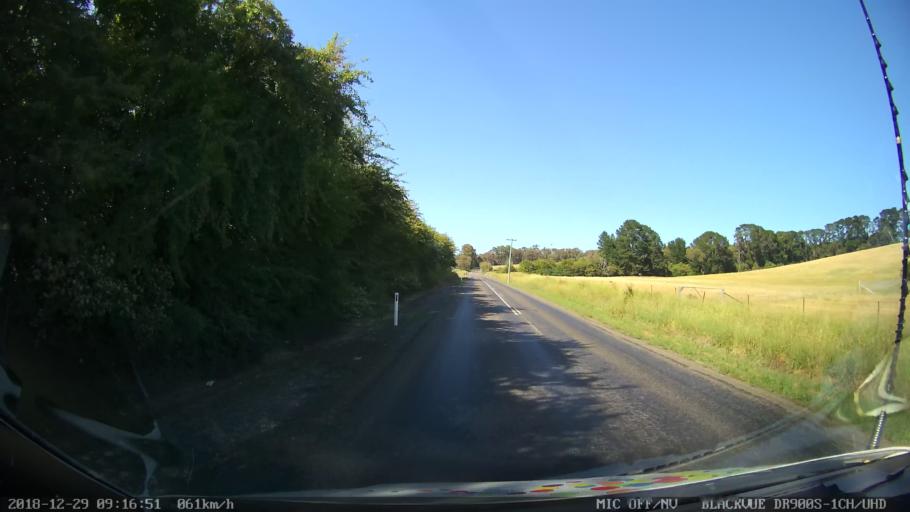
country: AU
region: New South Wales
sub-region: Upper Lachlan Shire
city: Crookwell
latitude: -34.4617
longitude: 149.4490
